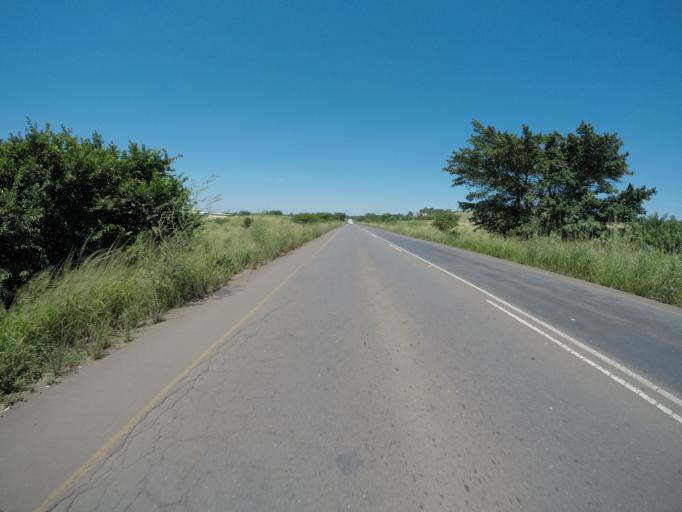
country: ZA
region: KwaZulu-Natal
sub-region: uThungulu District Municipality
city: Empangeni
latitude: -28.7319
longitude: 31.8739
